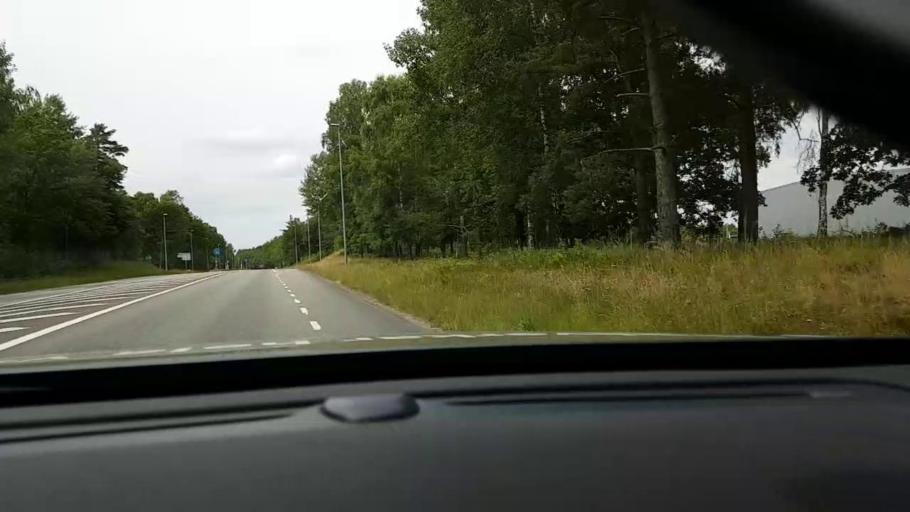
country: SE
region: Skane
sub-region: Hassleholms Kommun
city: Hassleholm
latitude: 56.1636
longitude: 13.7344
